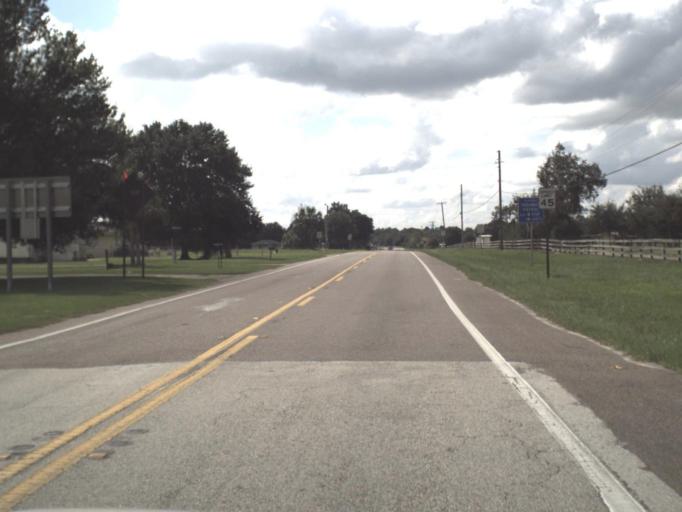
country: US
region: Florida
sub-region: Hardee County
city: Zolfo Springs
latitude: 27.5002
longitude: -81.8009
